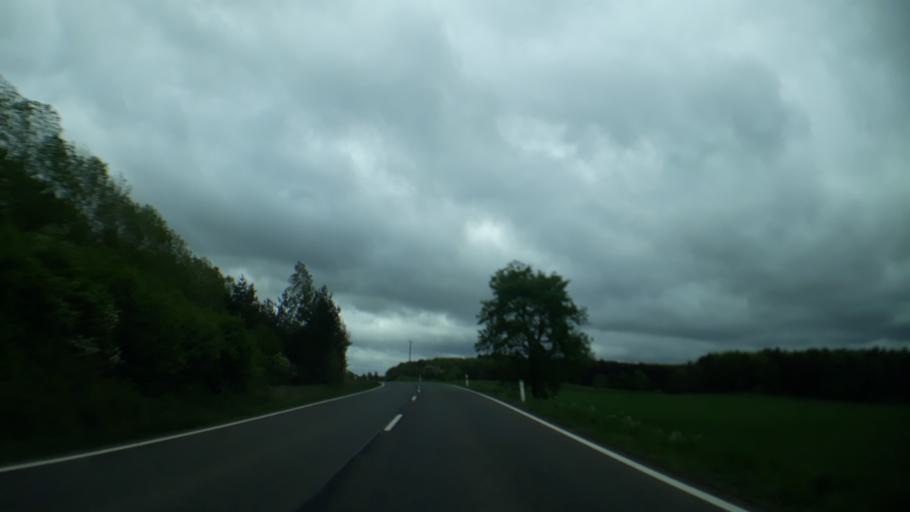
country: DE
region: North Rhine-Westphalia
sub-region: Regierungsbezirk Koln
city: Kall
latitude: 50.5282
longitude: 6.5867
